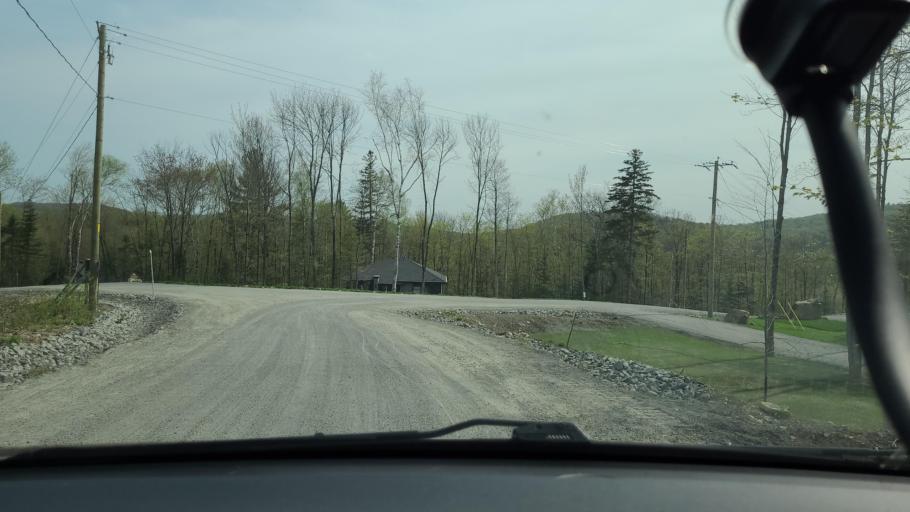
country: CA
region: Quebec
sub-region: Laurentides
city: Prevost
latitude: 45.8982
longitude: -74.0232
